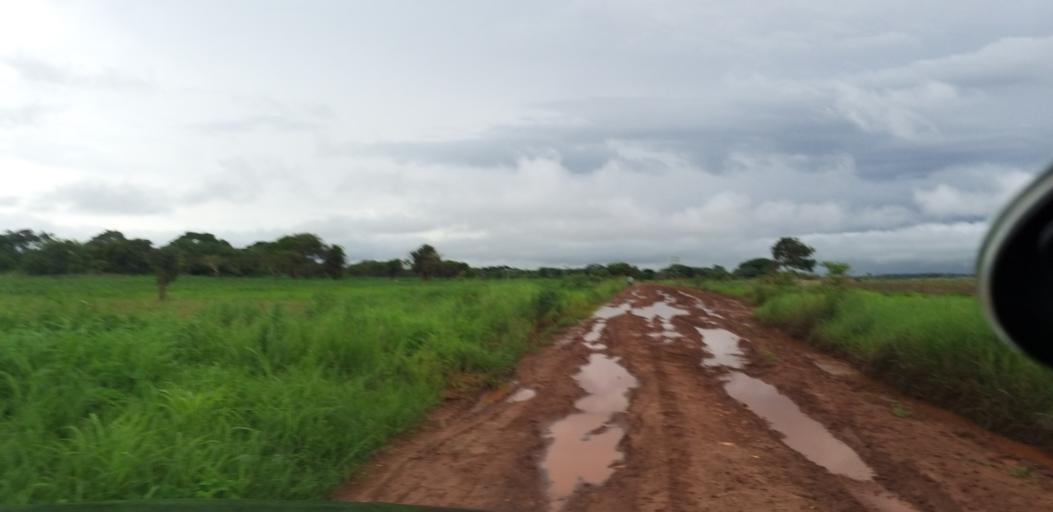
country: ZM
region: Lusaka
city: Lusaka
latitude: -15.5216
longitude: 28.3104
